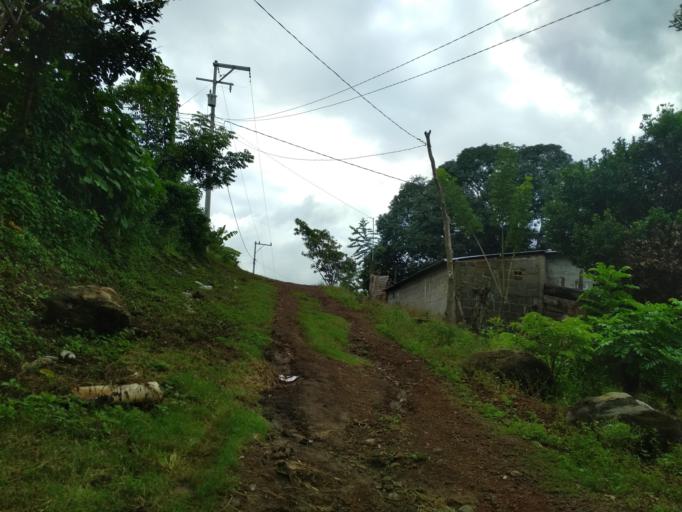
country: MX
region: Veracruz
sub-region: San Andres Tuxtla
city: Cerro las Iguanas
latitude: 18.4133
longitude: -95.2003
